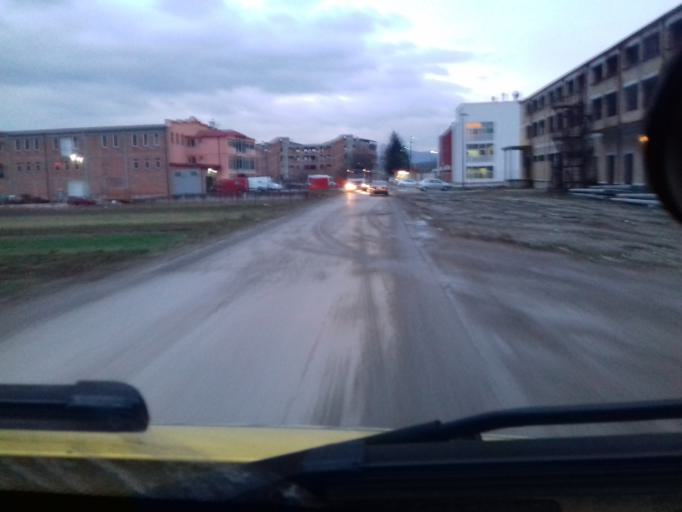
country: BA
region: Federation of Bosnia and Herzegovina
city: Visoko
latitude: 44.0019
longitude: 18.1752
